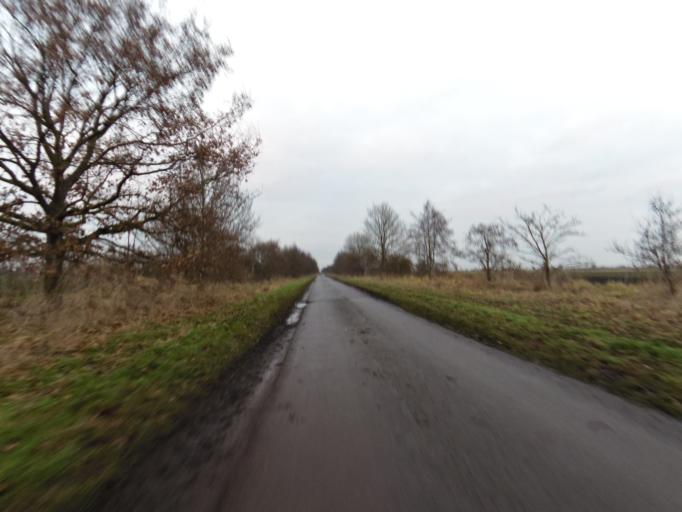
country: GB
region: England
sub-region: Cambridgeshire
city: Bottisham
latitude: 52.2707
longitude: 0.2613
